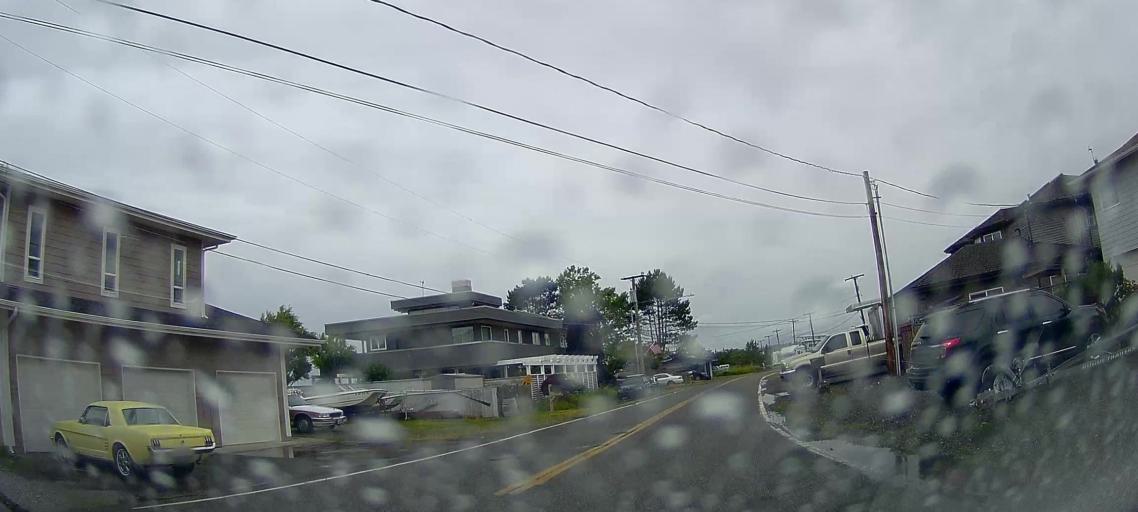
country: US
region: Washington
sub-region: Whatcom County
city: Marietta
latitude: 48.7899
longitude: -122.7103
